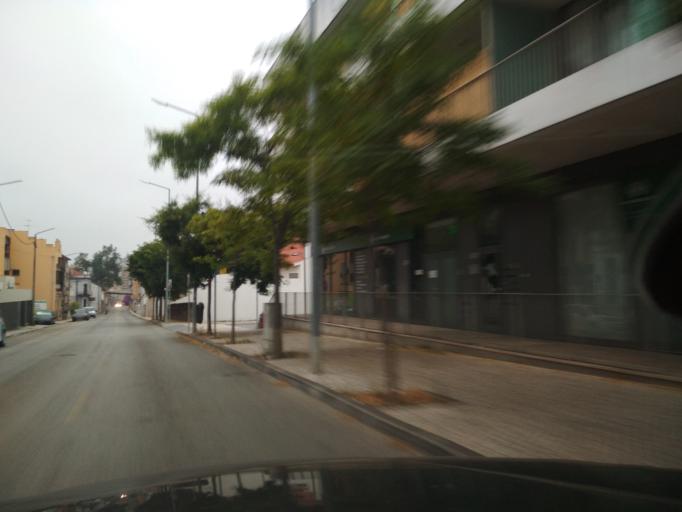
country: PT
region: Coimbra
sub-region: Coimbra
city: Coimbra
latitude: 40.2003
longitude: -8.4046
